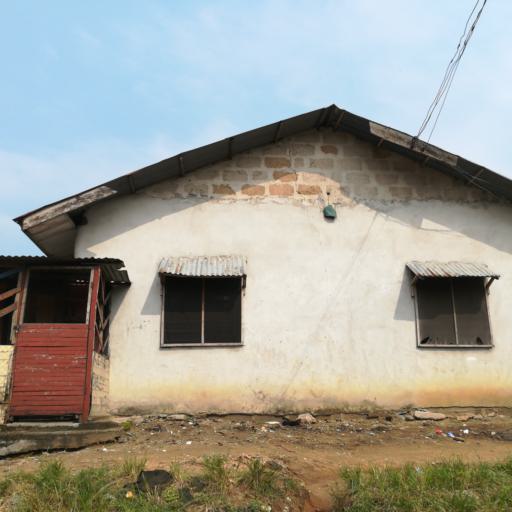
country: NG
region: Rivers
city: Port Harcourt
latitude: 4.8402
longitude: 7.0646
